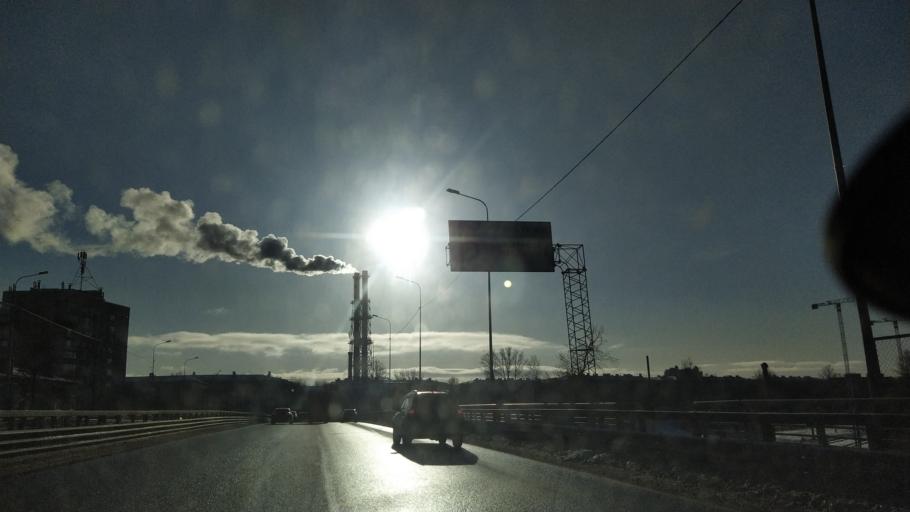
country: RU
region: Leningrad
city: Chernaya Rechka
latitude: 59.9925
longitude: 30.2988
